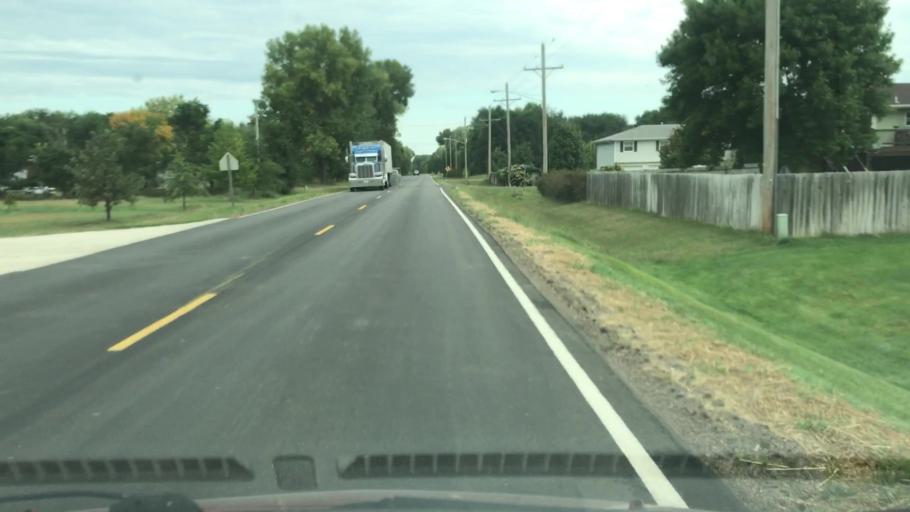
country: US
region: Nebraska
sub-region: Hall County
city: Grand Island
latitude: 40.9183
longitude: -98.3017
